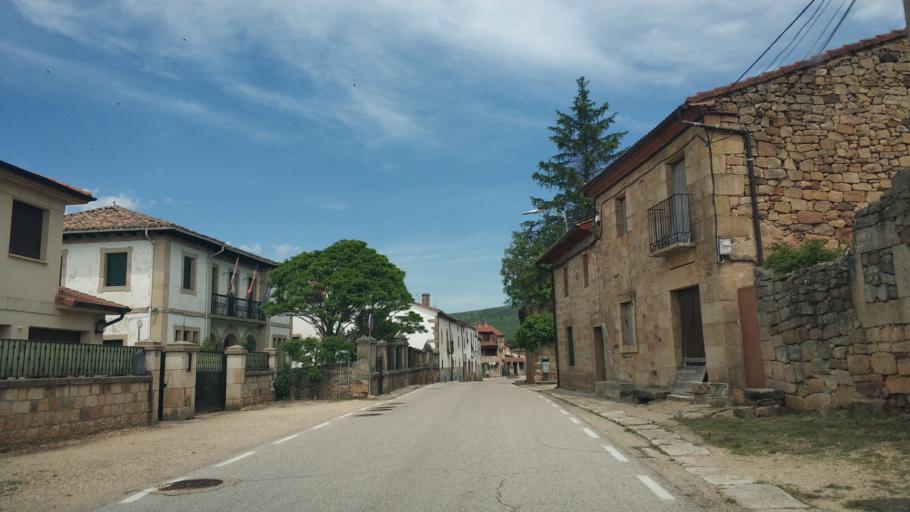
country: ES
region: Castille and Leon
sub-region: Provincia de Soria
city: Sotillo del Rincon
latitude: 41.9067
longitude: -2.6451
